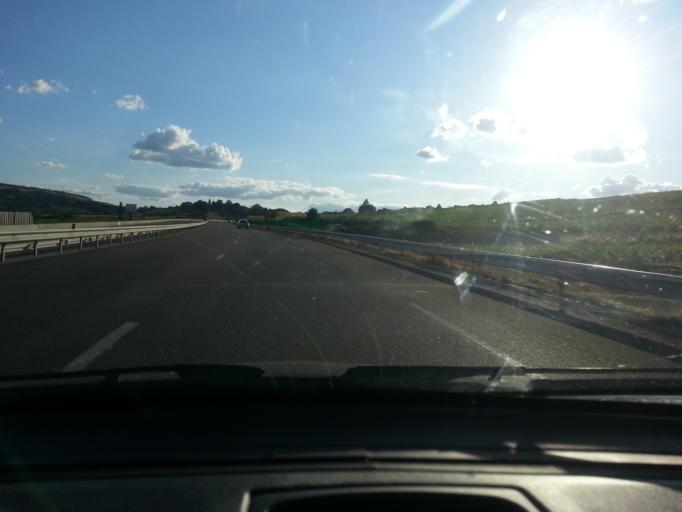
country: FR
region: Bourgogne
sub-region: Departement de Saone-et-Loire
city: Buxy
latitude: 46.7564
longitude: 4.6973
